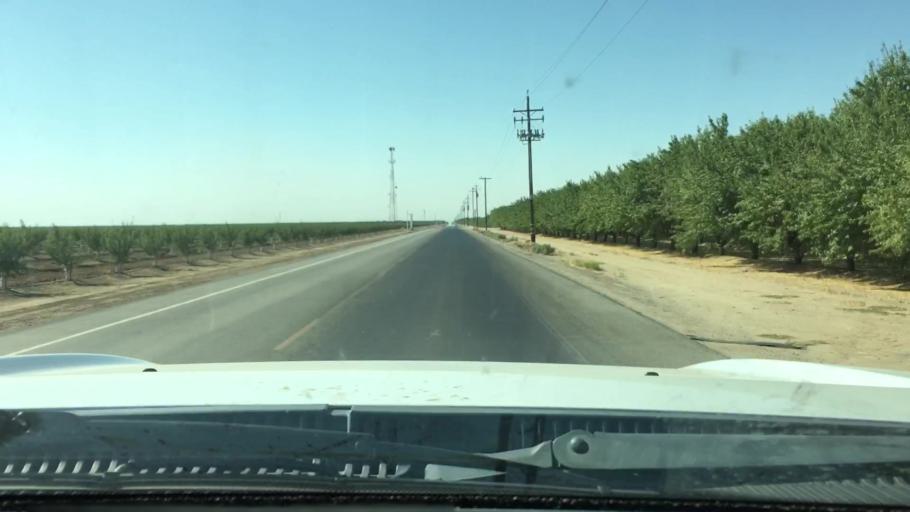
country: US
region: California
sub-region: Kern County
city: Wasco
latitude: 35.5926
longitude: -119.4737
